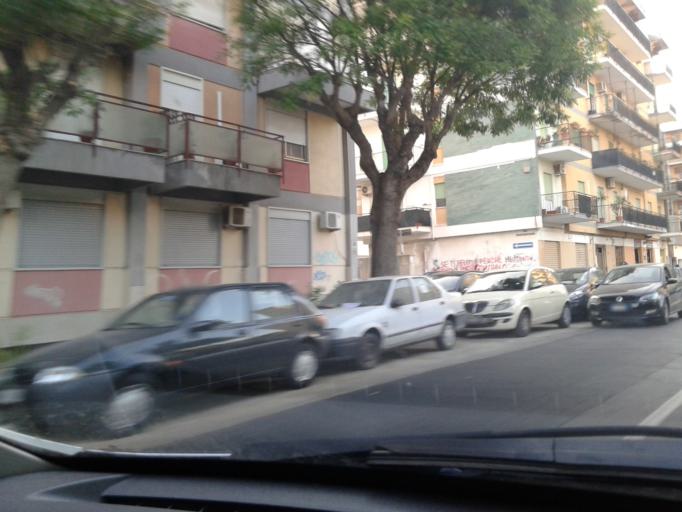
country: IT
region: Sicily
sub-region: Palermo
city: Palermo
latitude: 38.1040
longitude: 13.3355
